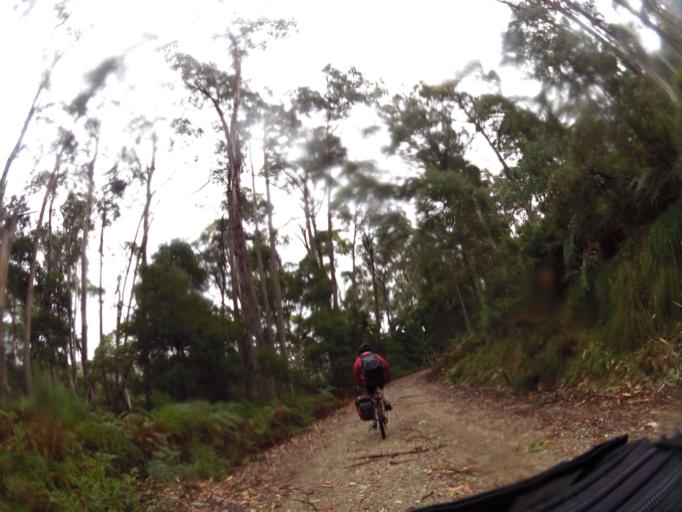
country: AU
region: New South Wales
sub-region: Greater Hume Shire
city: Holbrook
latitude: -36.1947
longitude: 147.5161
